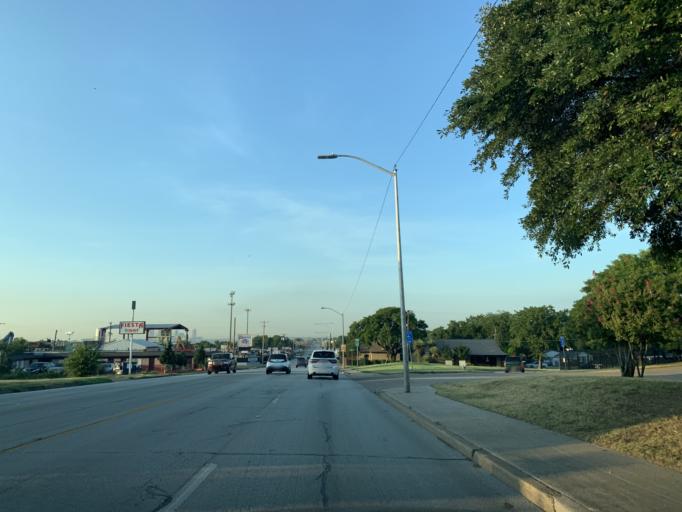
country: US
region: Texas
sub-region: Tarrant County
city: Blue Mound
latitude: 32.8136
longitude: -97.3515
